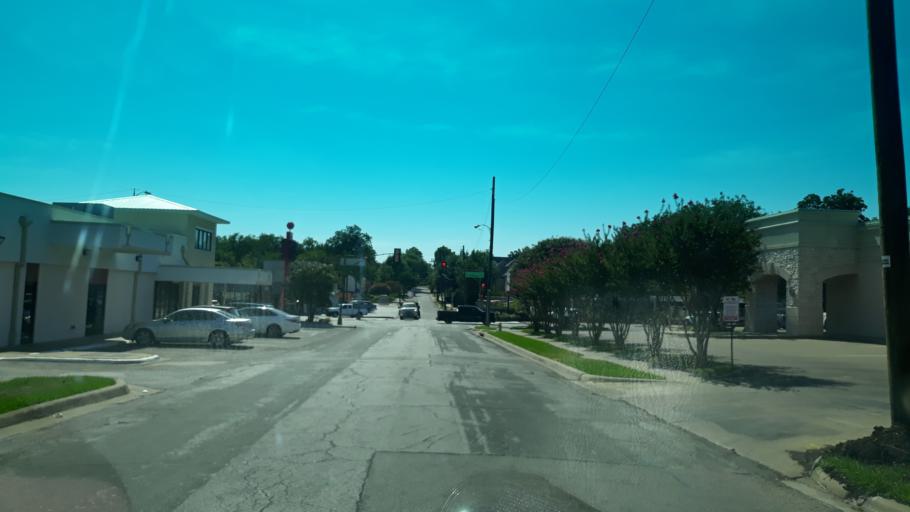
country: US
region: Texas
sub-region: Dallas County
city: Highland Park
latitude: 32.8139
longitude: -96.7608
